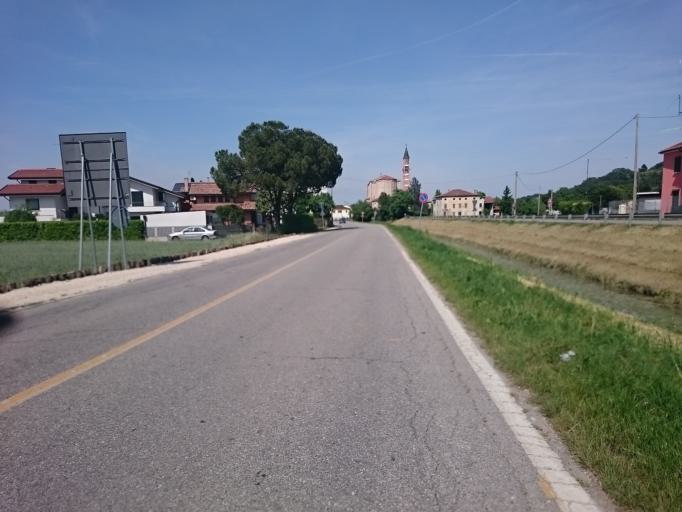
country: IT
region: Veneto
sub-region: Provincia di Padova
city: Bastia
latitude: 45.3825
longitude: 11.6491
